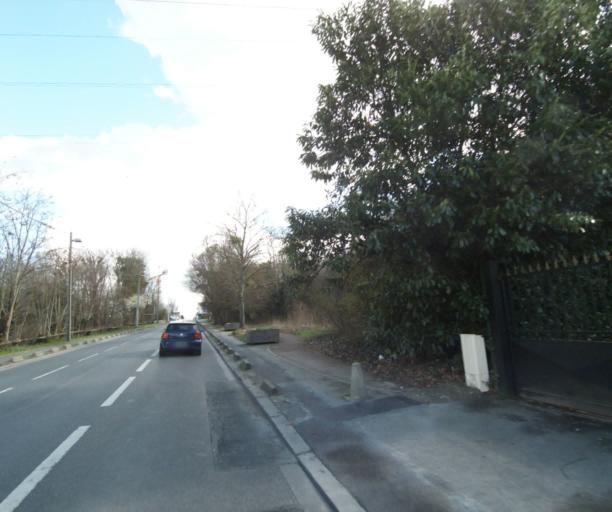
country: FR
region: Ile-de-France
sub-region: Departement de Seine-Saint-Denis
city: Villetaneuse
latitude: 48.9640
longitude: 2.3493
